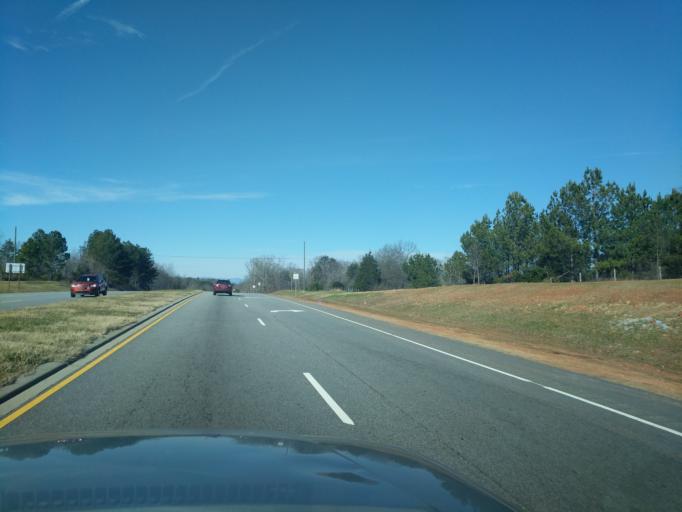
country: US
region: North Carolina
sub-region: Rutherford County
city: Spindale
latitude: 35.3085
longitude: -81.9231
